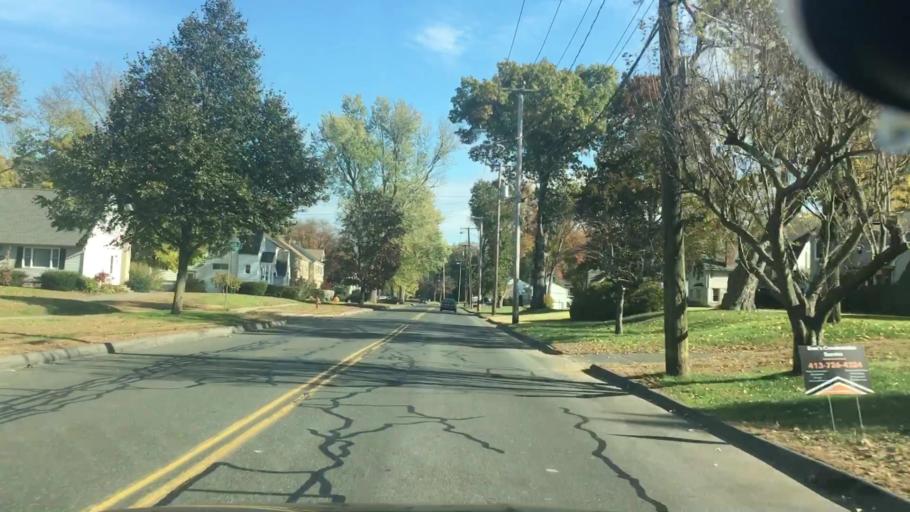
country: US
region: Massachusetts
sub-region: Hampden County
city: Longmeadow
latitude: 42.0325
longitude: -72.5796
